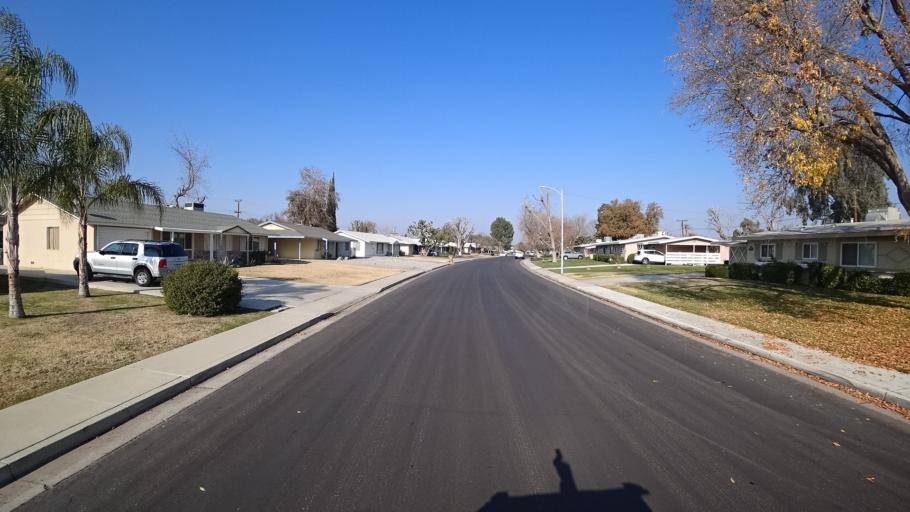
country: US
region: California
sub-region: Kern County
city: Greenacres
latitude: 35.3461
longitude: -119.0713
